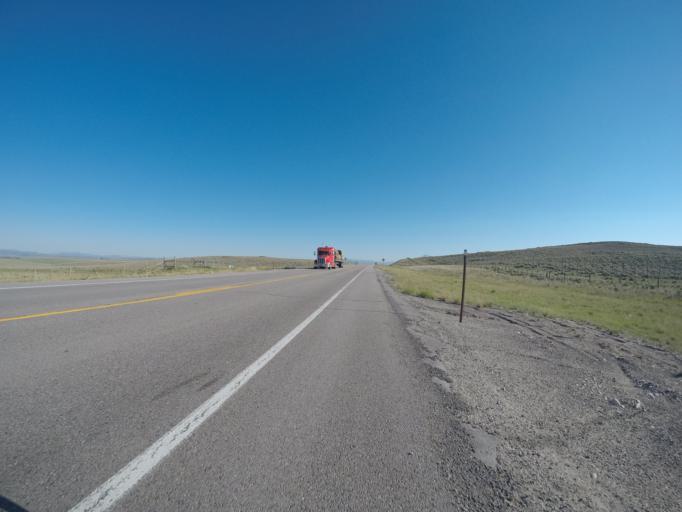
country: US
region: Wyoming
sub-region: Sublette County
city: Pinedale
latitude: 42.9187
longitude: -110.0798
